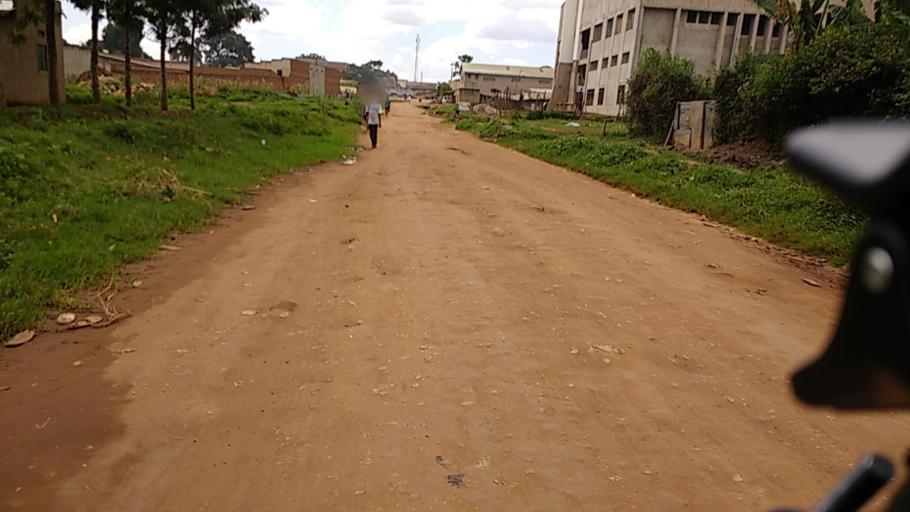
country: UG
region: Eastern Region
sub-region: Mbale District
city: Mbale
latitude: 1.0734
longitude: 34.1640
